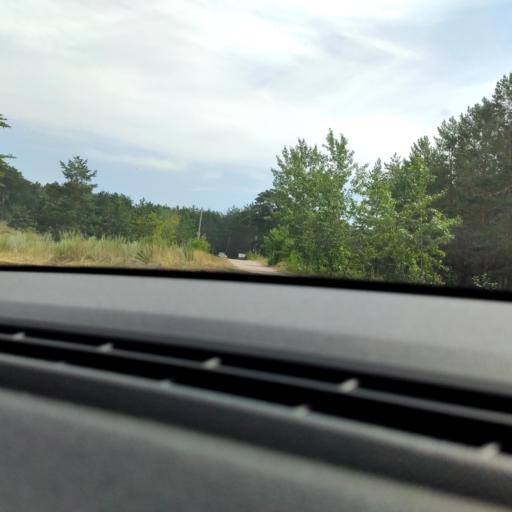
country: RU
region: Samara
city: Tol'yatti
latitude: 53.4707
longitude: 49.3686
